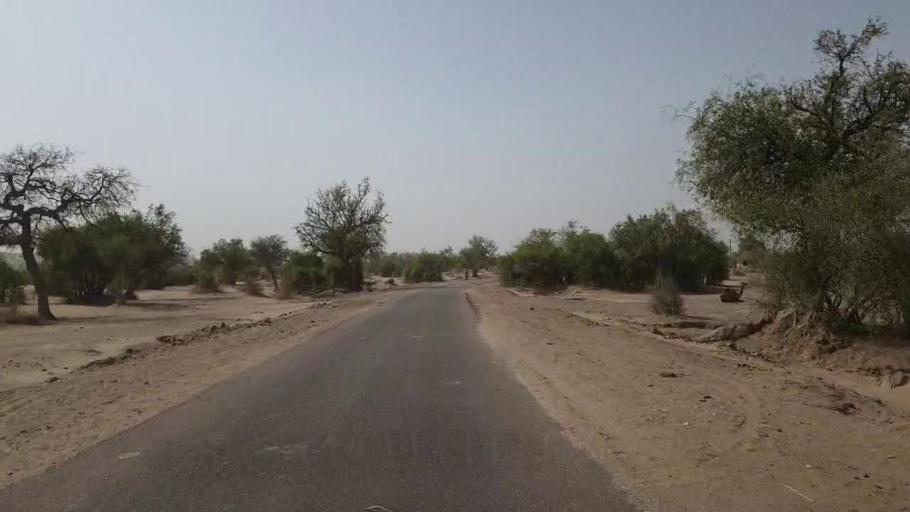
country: PK
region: Sindh
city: Mithi
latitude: 24.6085
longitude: 69.9208
